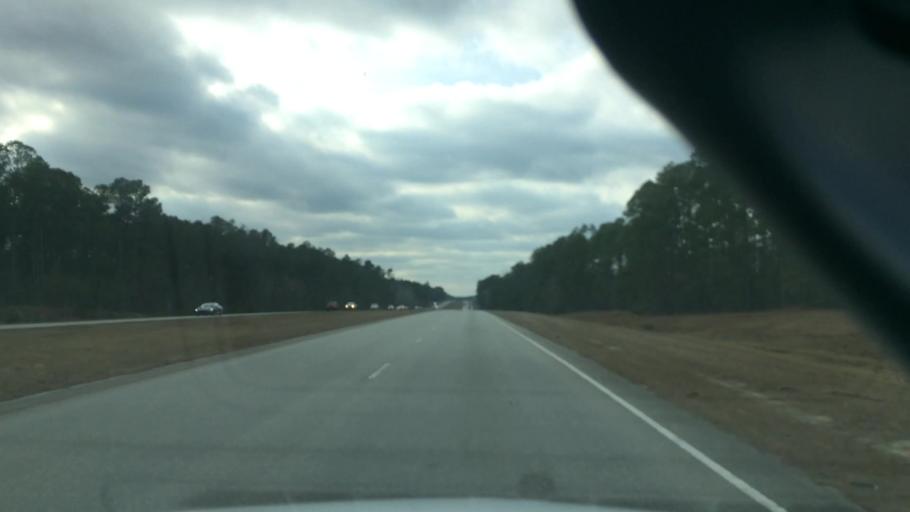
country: US
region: North Carolina
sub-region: Brunswick County
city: Bolivia
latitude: 34.0480
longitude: -78.2256
